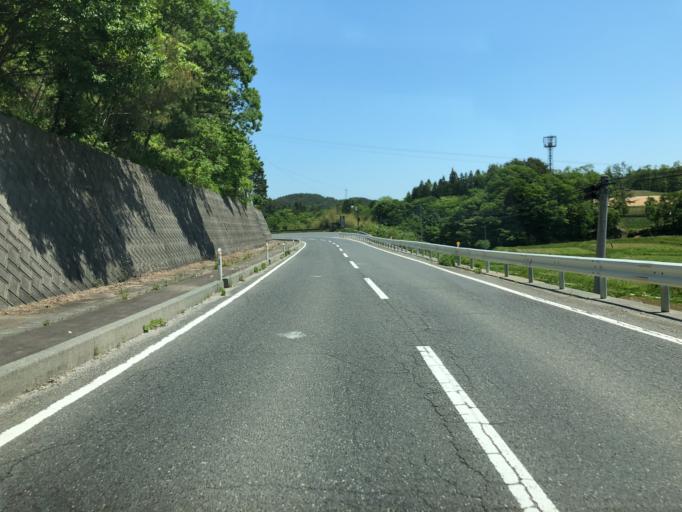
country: JP
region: Fukushima
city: Funehikimachi-funehiki
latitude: 37.5025
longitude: 140.7545
